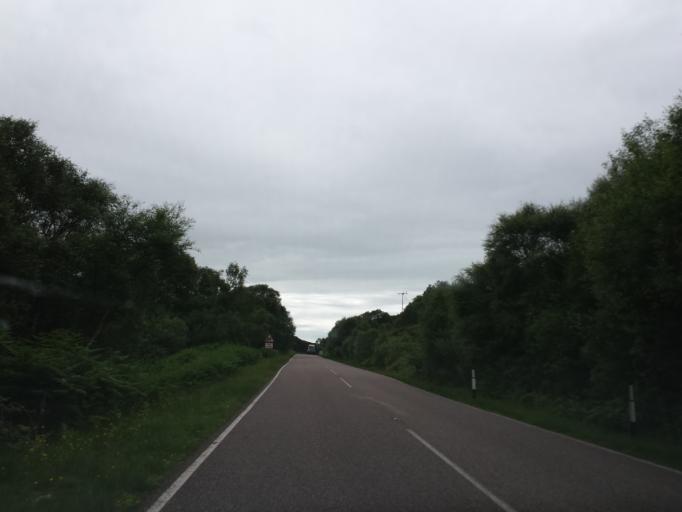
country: GB
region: Scotland
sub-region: Argyll and Bute
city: Isle Of Mull
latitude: 56.8843
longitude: -5.6546
